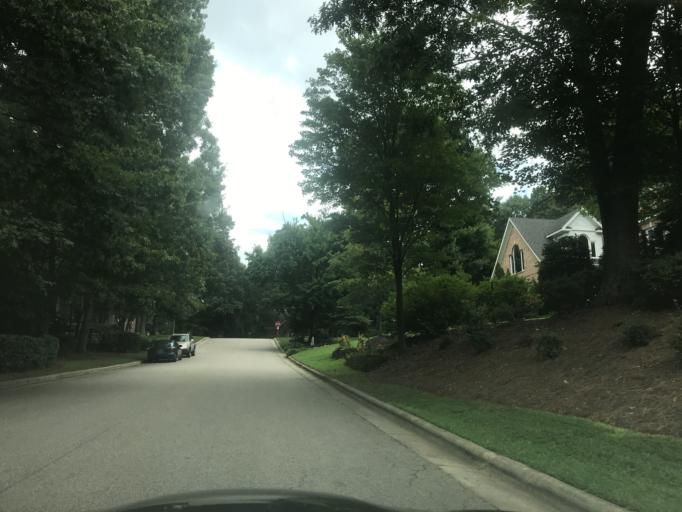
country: US
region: North Carolina
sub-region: Wake County
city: West Raleigh
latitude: 35.8879
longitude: -78.6067
